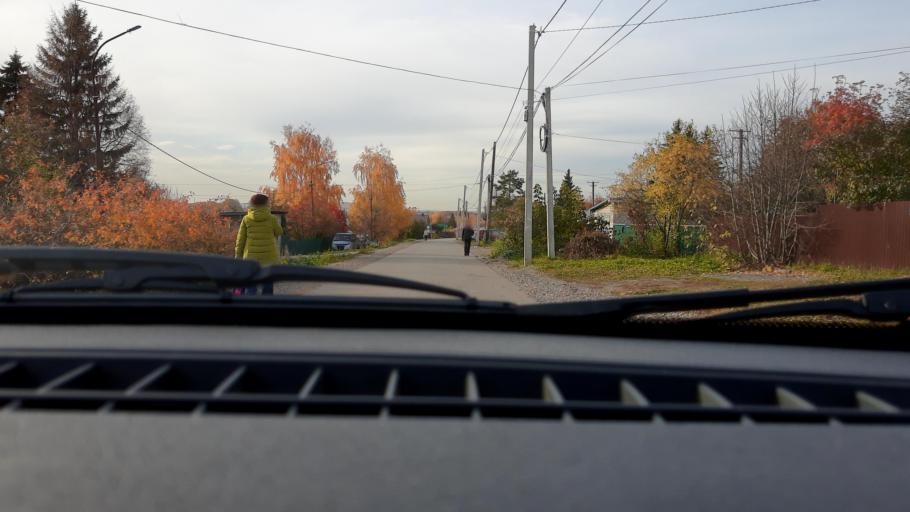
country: RU
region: Bashkortostan
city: Mikhaylovka
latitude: 54.8105
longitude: 55.8962
